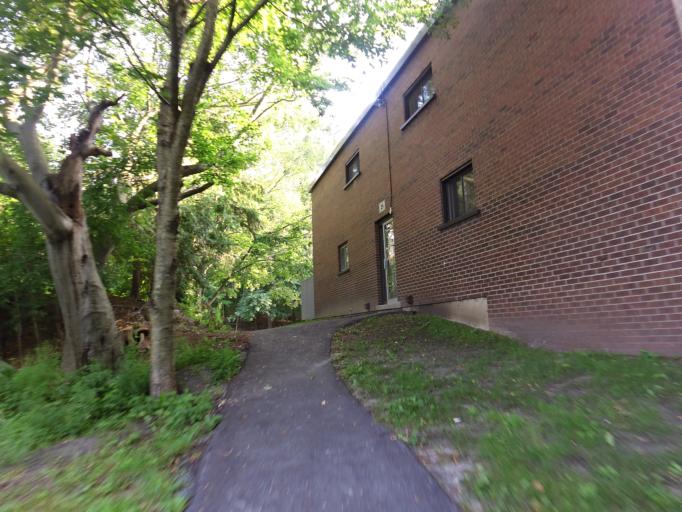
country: CA
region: Ontario
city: Bells Corners
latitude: 45.3421
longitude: -75.7777
